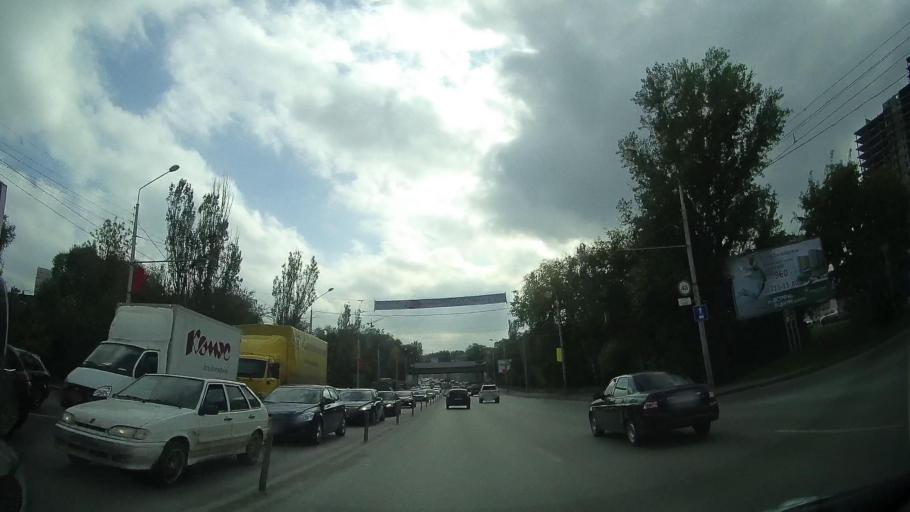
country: RU
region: Rostov
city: Rostov-na-Donu
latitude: 47.2469
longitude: 39.6968
